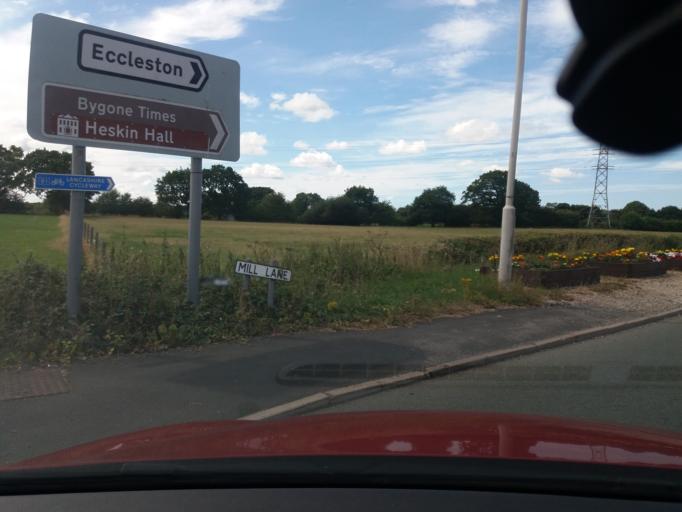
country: GB
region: England
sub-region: Lancashire
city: Coppull
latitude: 53.6292
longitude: -2.6856
